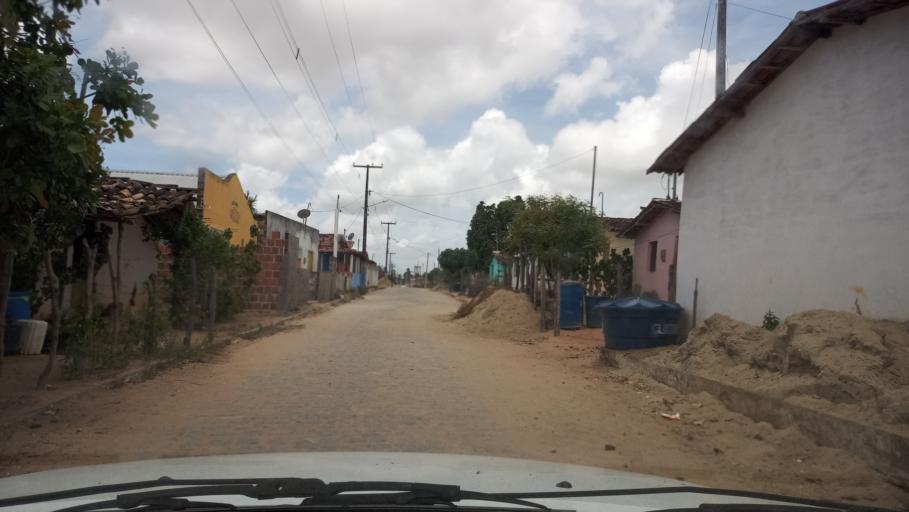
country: BR
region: Rio Grande do Norte
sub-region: Goianinha
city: Goianinha
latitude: -6.2898
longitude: -35.2819
